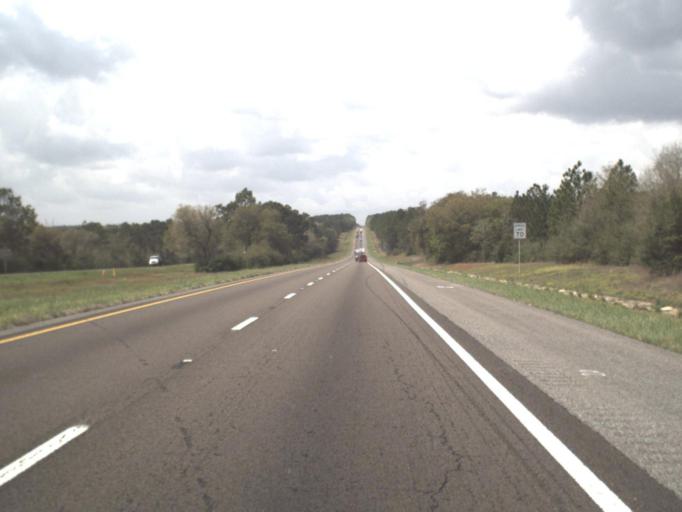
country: US
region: Florida
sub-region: Okaloosa County
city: Crestview
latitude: 30.6953
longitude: -86.7610
